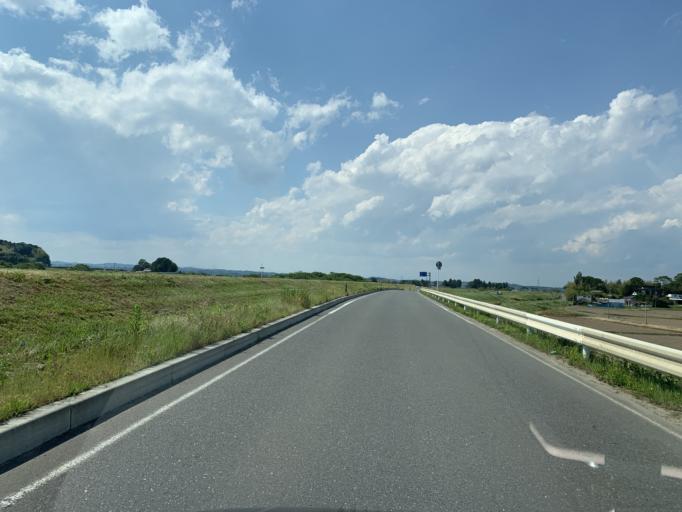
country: JP
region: Miyagi
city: Matsushima
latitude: 38.4369
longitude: 141.1185
